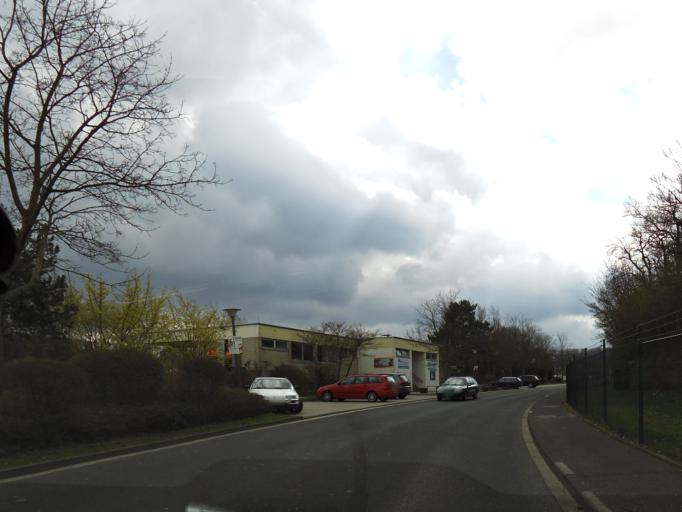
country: DE
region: North Rhine-Westphalia
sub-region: Regierungsbezirk Koln
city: Rheinbach
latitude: 50.6220
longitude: 6.9331
